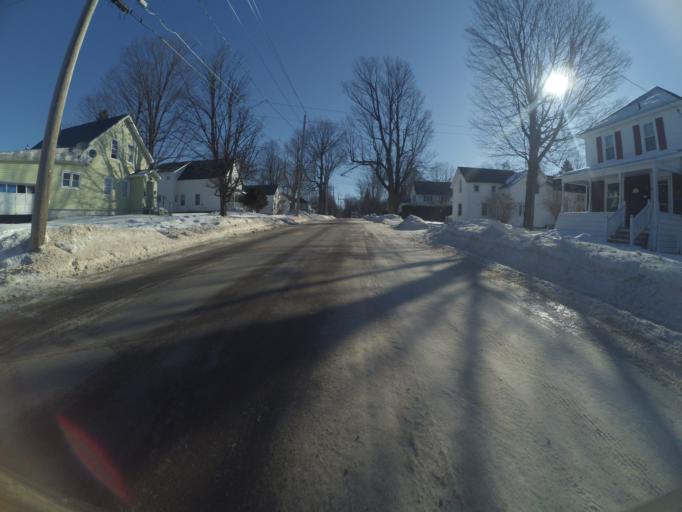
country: US
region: New York
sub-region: St. Lawrence County
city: Potsdam
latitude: 44.6779
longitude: -74.9895
